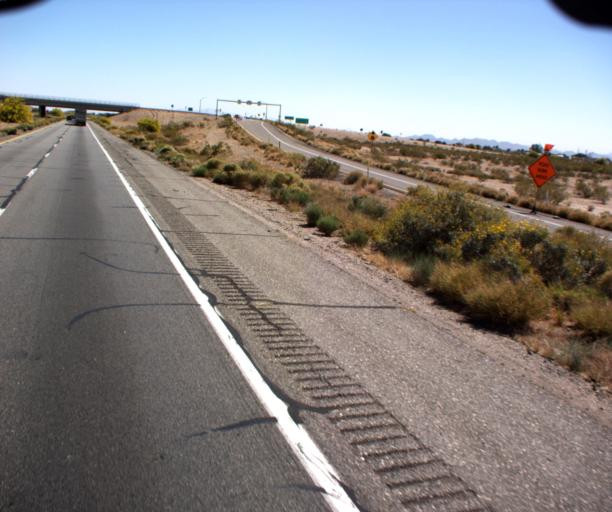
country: US
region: Arizona
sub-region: Maricopa County
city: Buckeye
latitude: 33.4398
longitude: -112.6808
